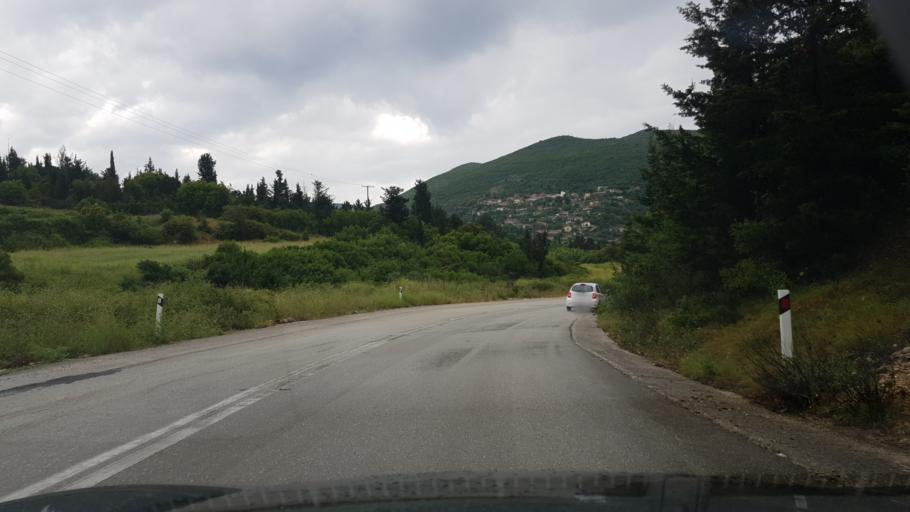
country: GR
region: Ionian Islands
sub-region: Lefkada
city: Nidri
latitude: 38.6297
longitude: 20.6363
